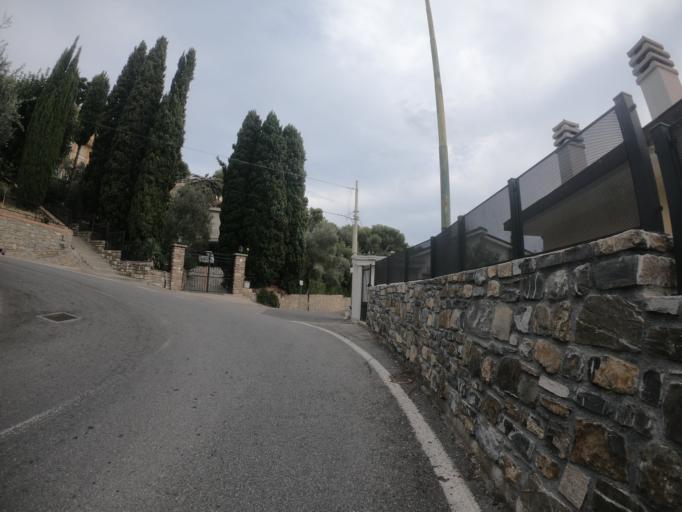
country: IT
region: Liguria
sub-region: Provincia di Savona
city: Marina di Andora
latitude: 43.9542
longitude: 8.1527
